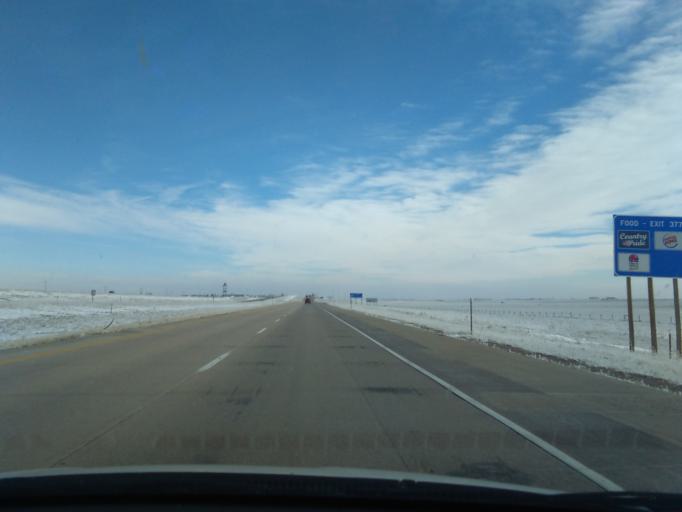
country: US
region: Wyoming
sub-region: Laramie County
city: Fox Farm-College
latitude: 41.1580
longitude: -104.5380
